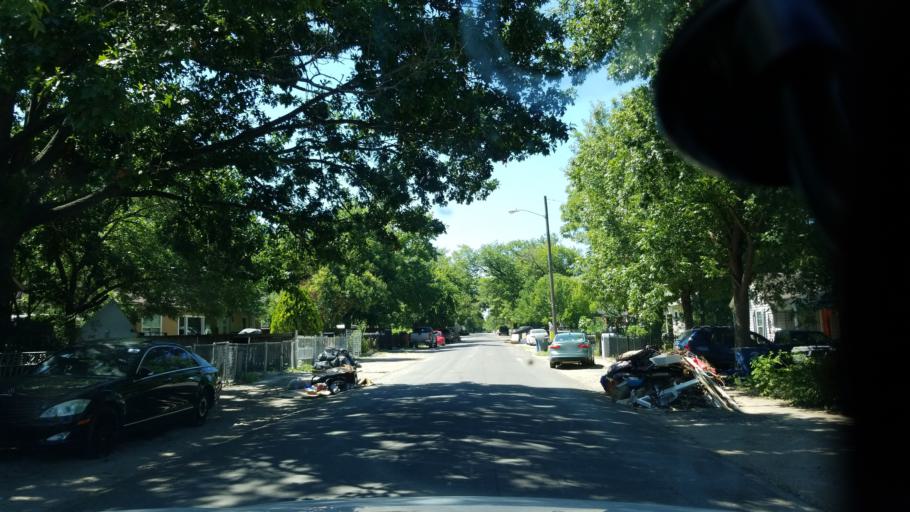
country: US
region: Texas
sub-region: Dallas County
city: Dallas
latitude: 32.7125
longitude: -96.8171
